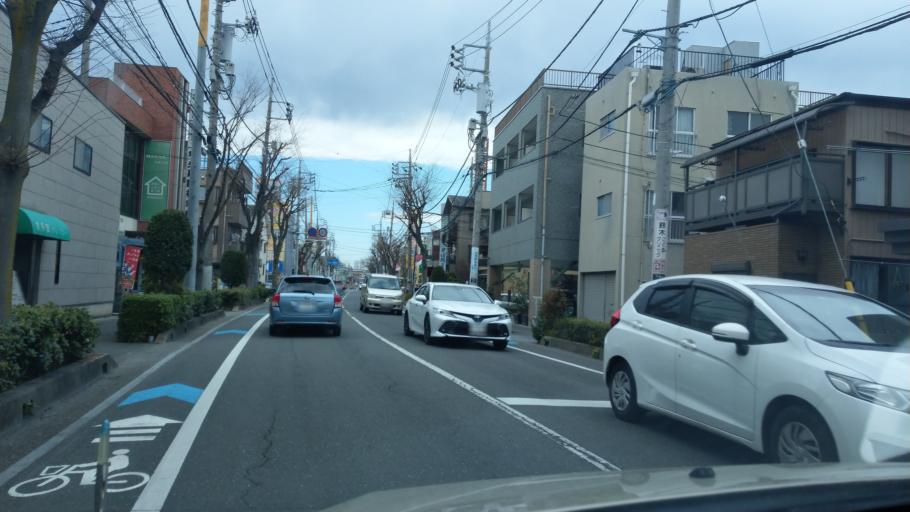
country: JP
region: Saitama
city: Yono
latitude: 35.8814
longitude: 139.6279
